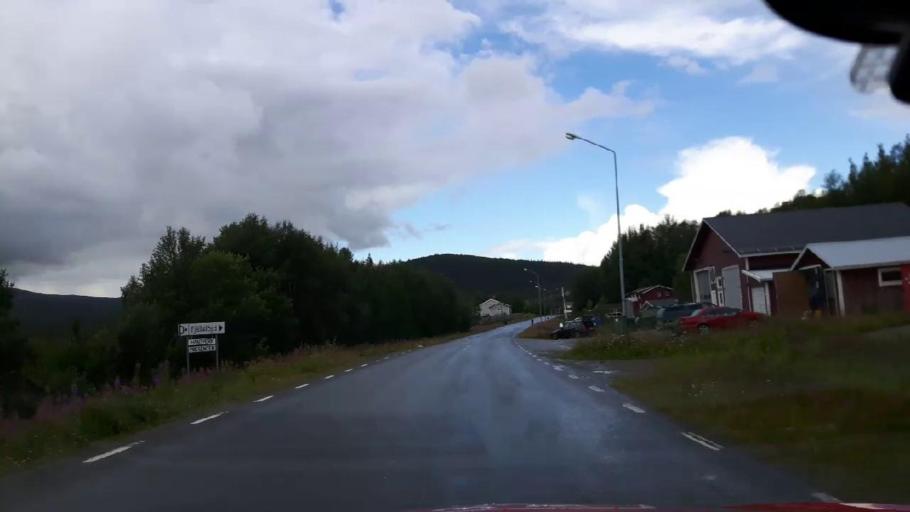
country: SE
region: Vaesterbotten
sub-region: Vilhelmina Kommun
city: Sjoberg
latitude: 64.9701
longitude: 15.3493
